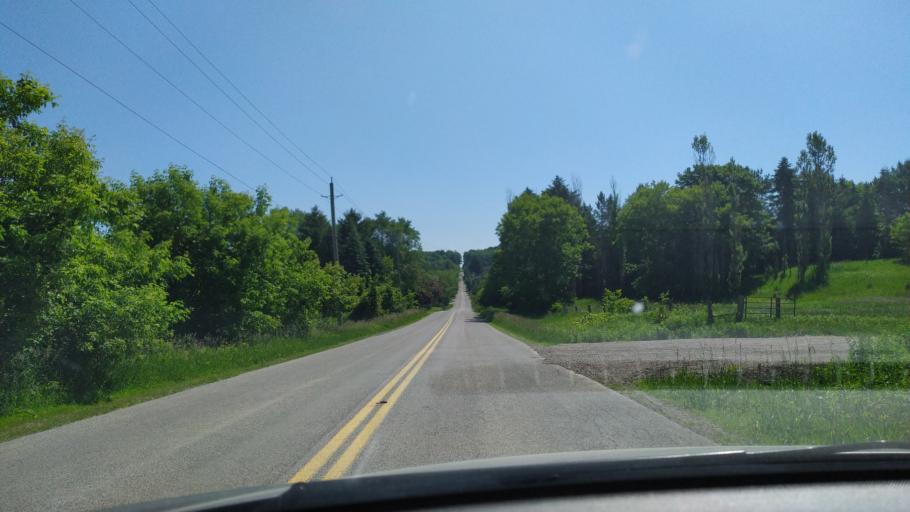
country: CA
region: Ontario
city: Waterloo
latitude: 43.4710
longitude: -80.6377
